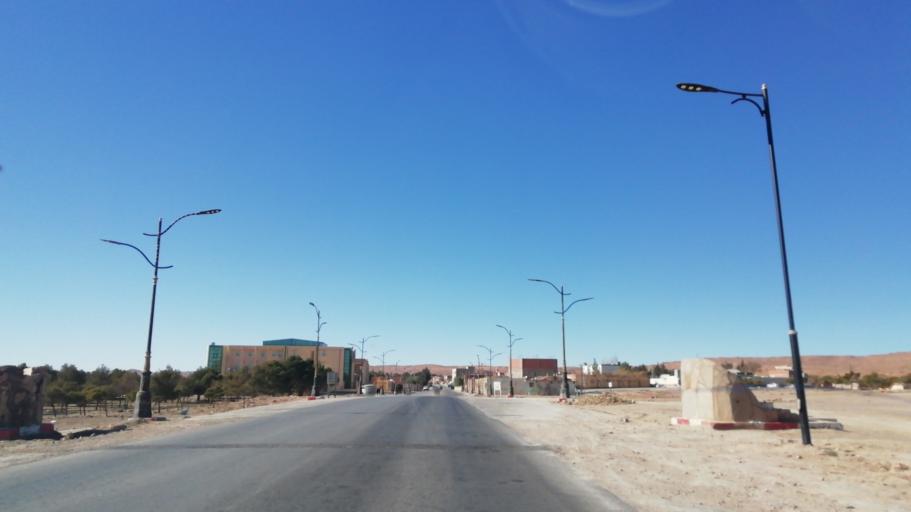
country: DZ
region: El Bayadh
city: El Bayadh
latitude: 33.7287
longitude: 1.5429
